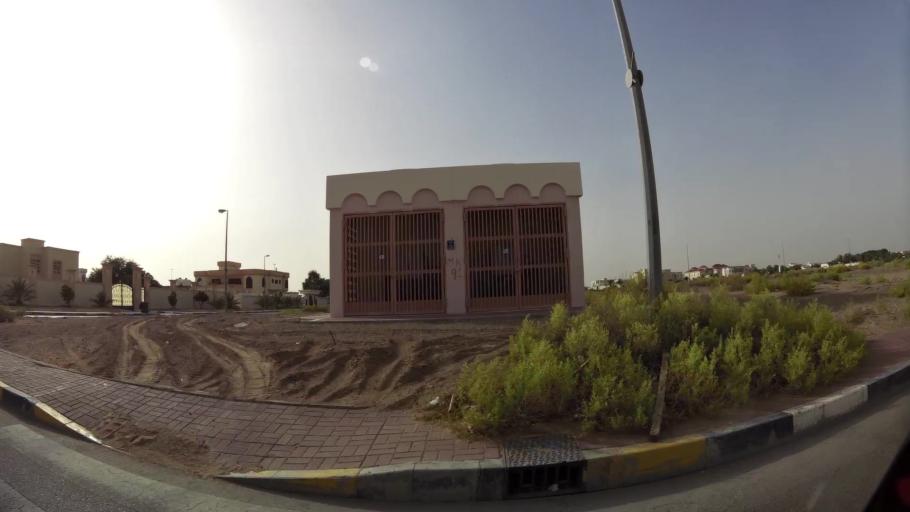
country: AE
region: Abu Dhabi
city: Al Ain
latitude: 24.2225
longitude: 55.6555
